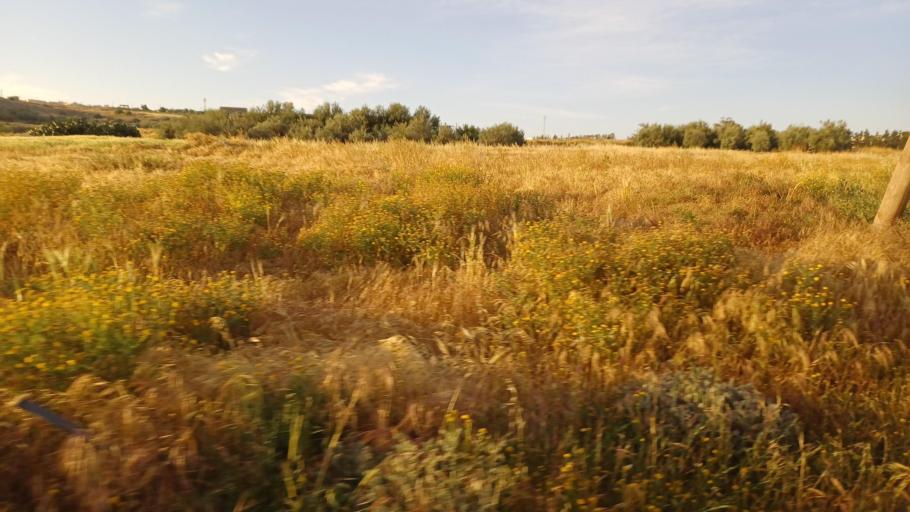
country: CY
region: Lefkosia
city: Akaki
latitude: 35.1706
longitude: 33.1517
